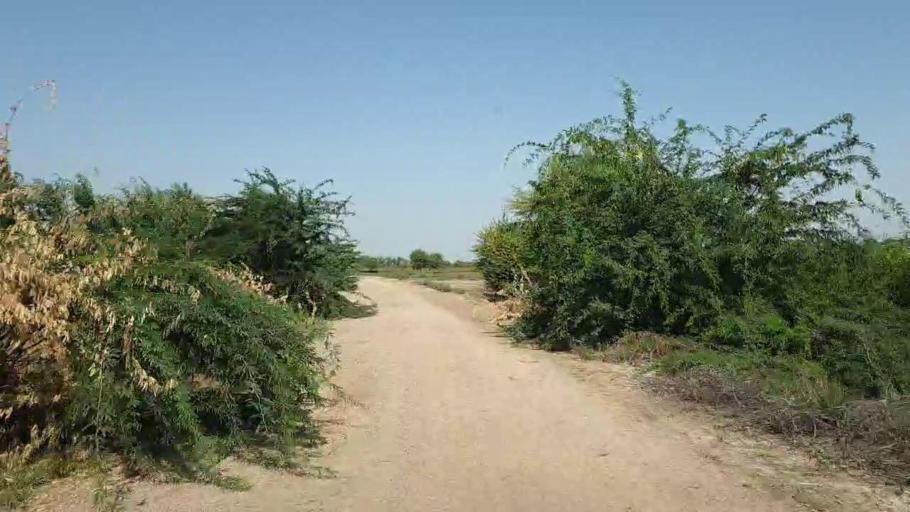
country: PK
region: Sindh
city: Tando Bago
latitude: 24.7349
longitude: 69.0430
